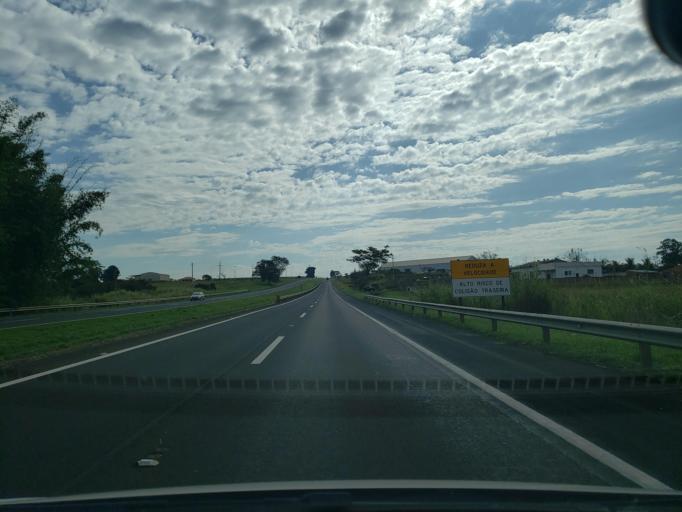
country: BR
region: Sao Paulo
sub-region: Lins
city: Lins
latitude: -21.6468
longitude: -49.8170
